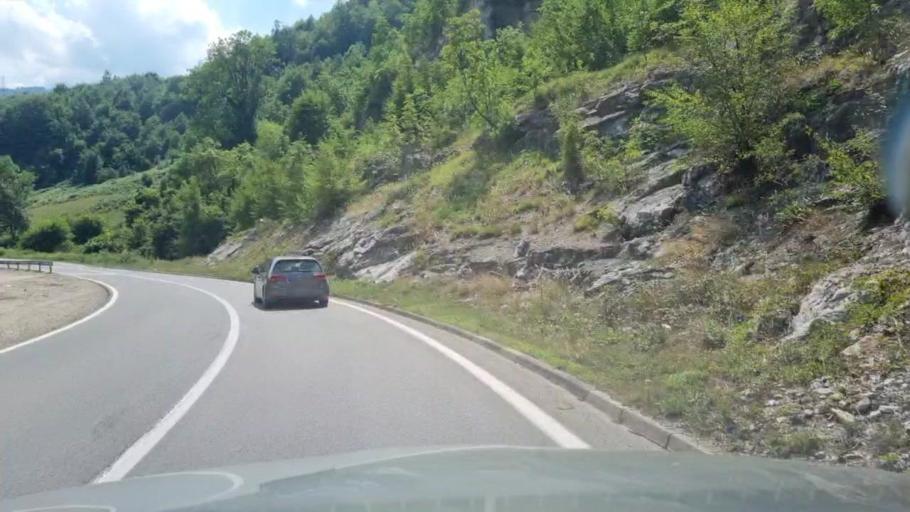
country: BA
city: Stupari
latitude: 44.3591
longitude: 18.6719
